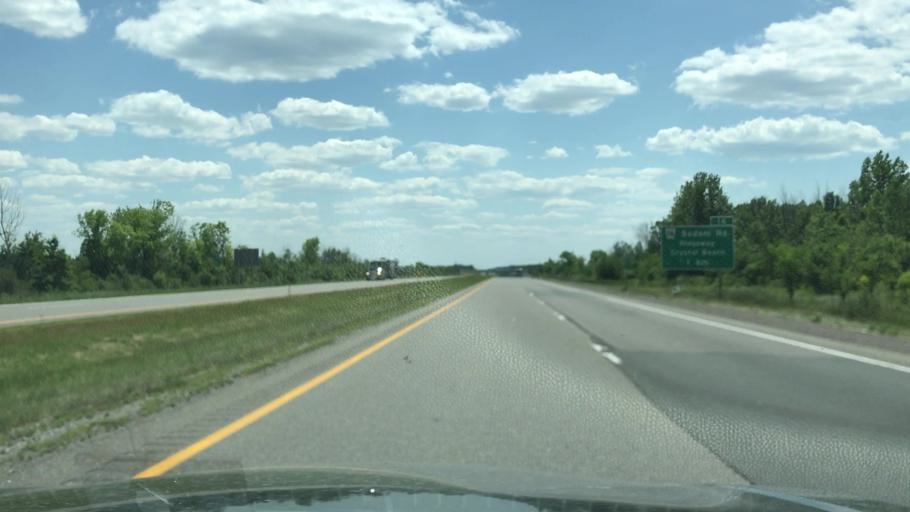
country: US
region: New York
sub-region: Niagara County
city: Niagara Falls
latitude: 42.9993
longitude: -79.0686
